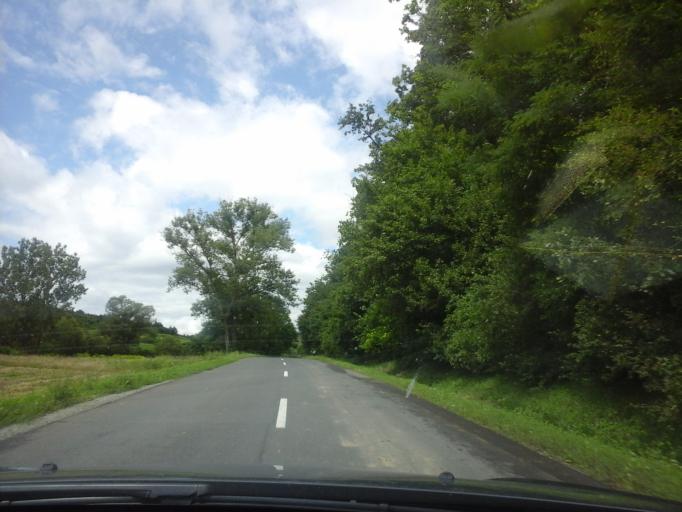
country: HU
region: Borsod-Abauj-Zemplen
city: Rudabanya
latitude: 48.4201
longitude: 20.5022
